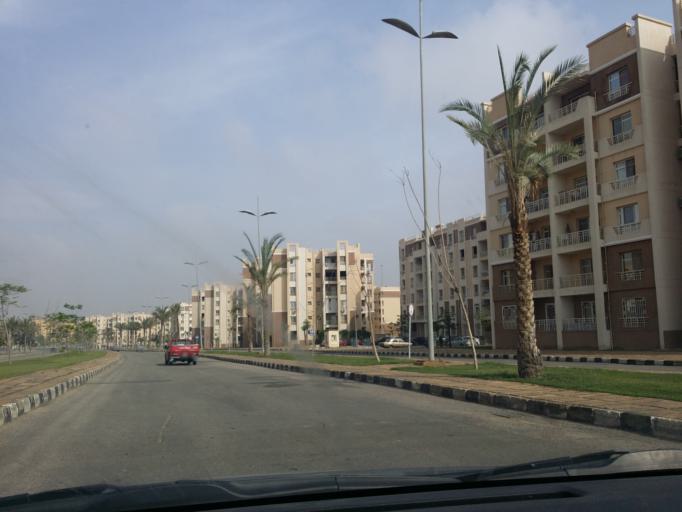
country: EG
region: Muhafazat al Qalyubiyah
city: Al Khankah
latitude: 30.0832
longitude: 31.6486
